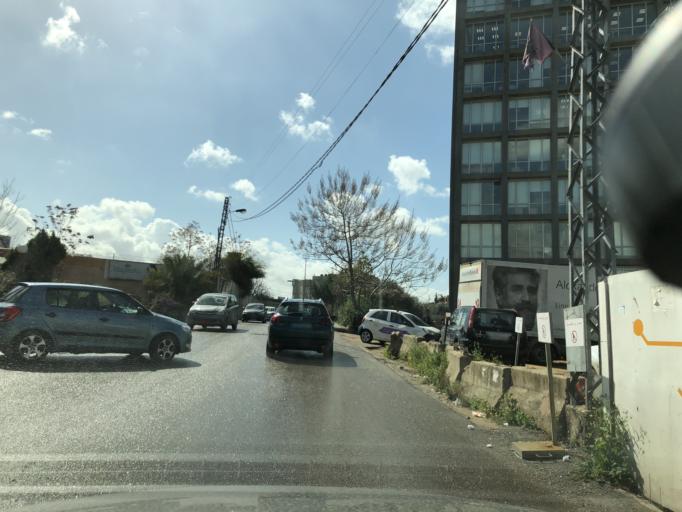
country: LB
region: Mont-Liban
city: Jdaidet el Matn
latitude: 33.8708
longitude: 35.5436
